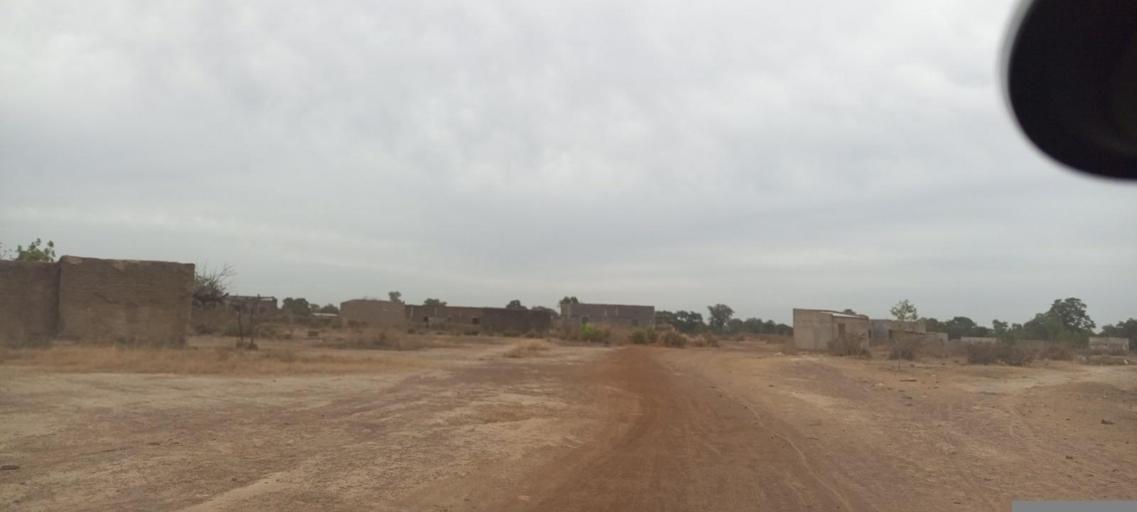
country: ML
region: Koulikoro
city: Kati
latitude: 12.7968
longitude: -8.2502
